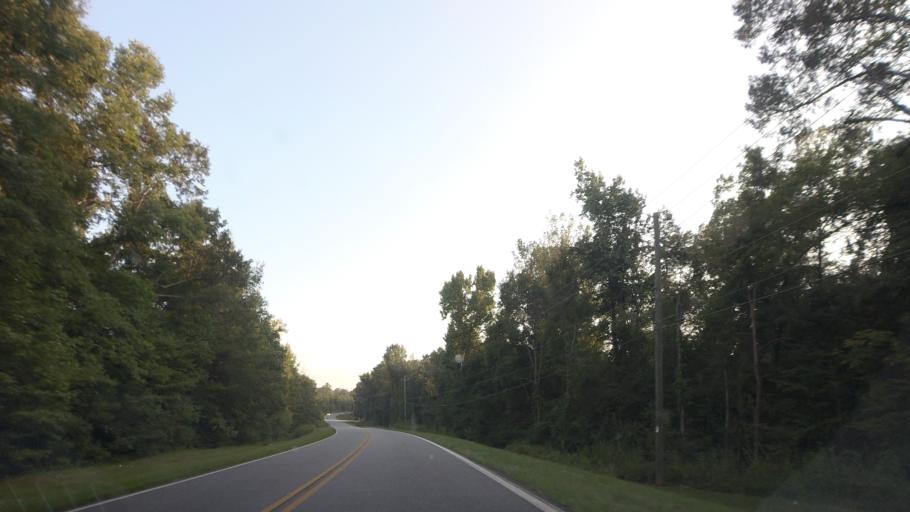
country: US
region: Georgia
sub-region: Bibb County
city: West Point
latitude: 32.8680
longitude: -83.7832
